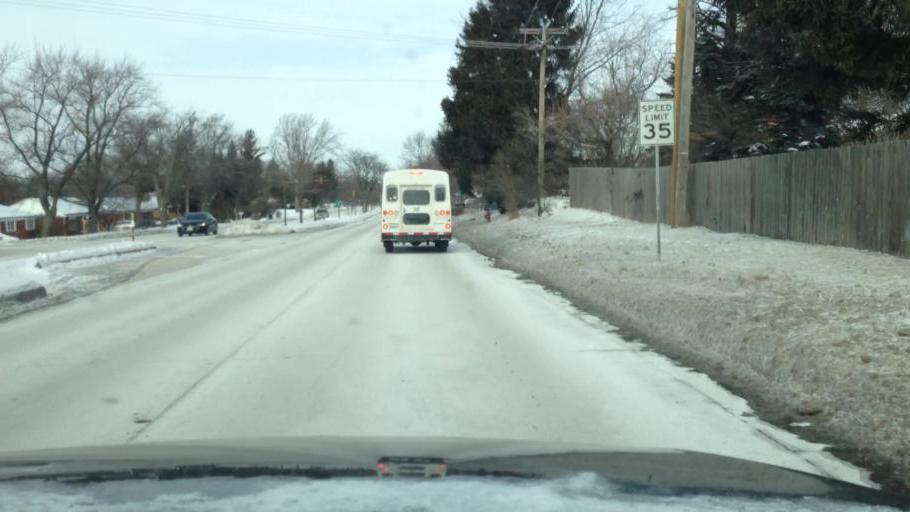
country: US
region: Illinois
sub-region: DuPage County
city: Lombard
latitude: 41.8524
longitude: -88.0119
